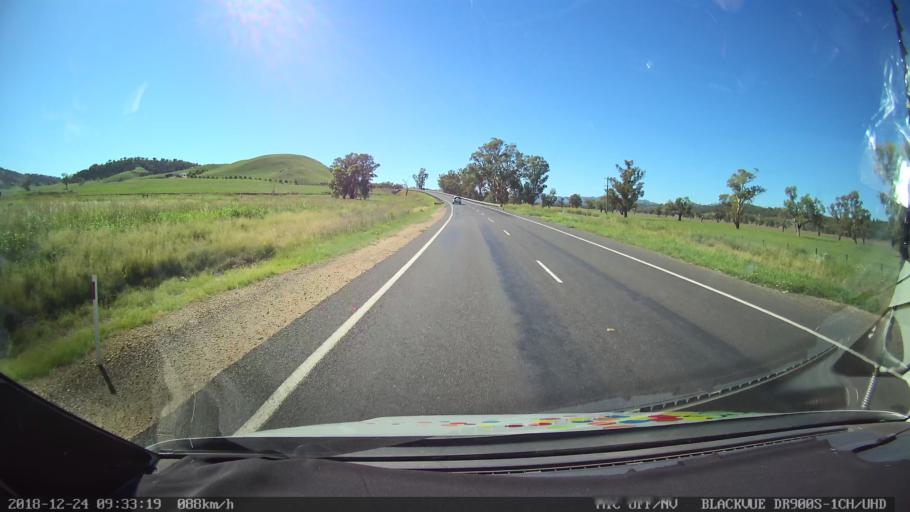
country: AU
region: New South Wales
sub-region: Liverpool Plains
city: Quirindi
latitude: -31.6021
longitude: 150.7065
